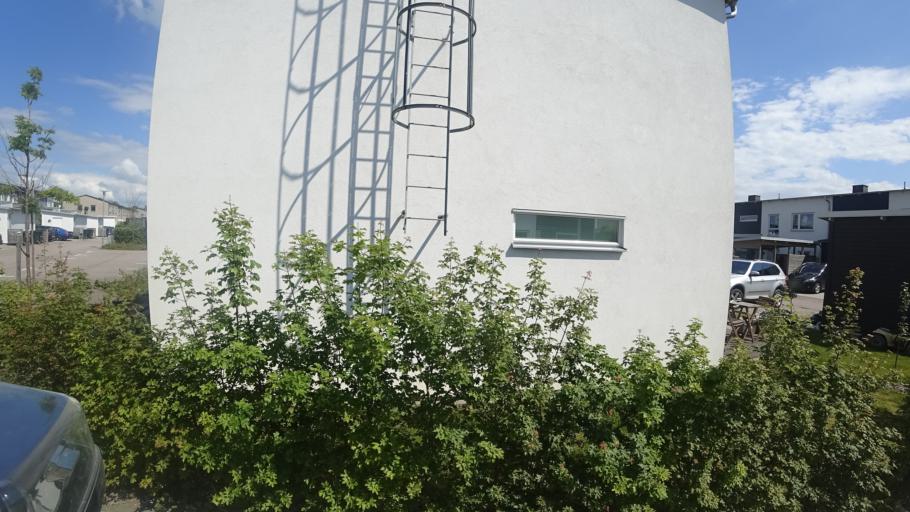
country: SE
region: Skane
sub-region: Lunds Kommun
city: Lund
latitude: 55.6897
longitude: 13.2358
